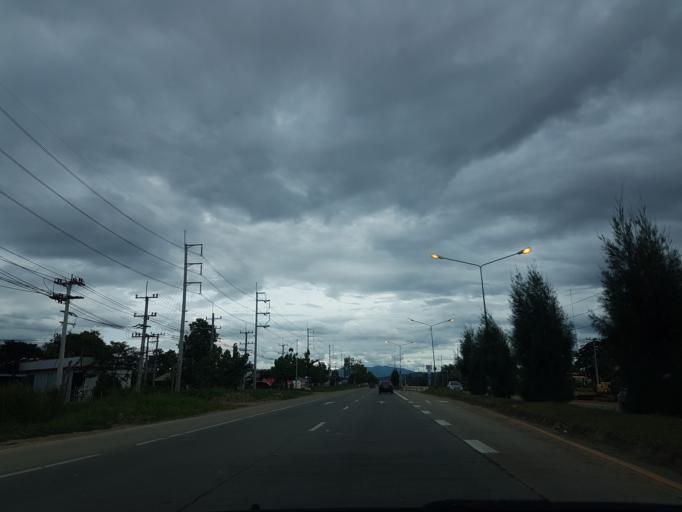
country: TH
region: Lamphun
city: Lamphun
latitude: 18.5751
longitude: 99.0436
